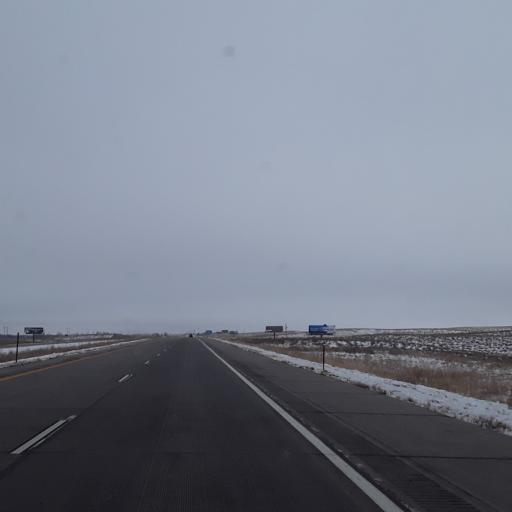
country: US
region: Colorado
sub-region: Logan County
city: Sterling
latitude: 40.5920
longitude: -103.1902
